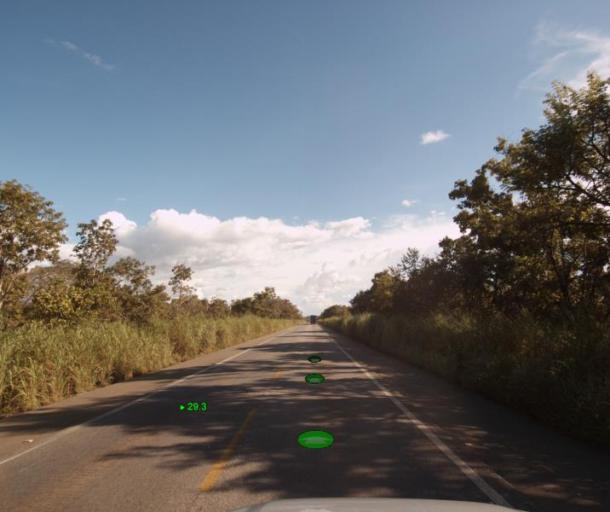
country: BR
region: Goias
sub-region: Porangatu
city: Porangatu
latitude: -13.0832
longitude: -49.1909
